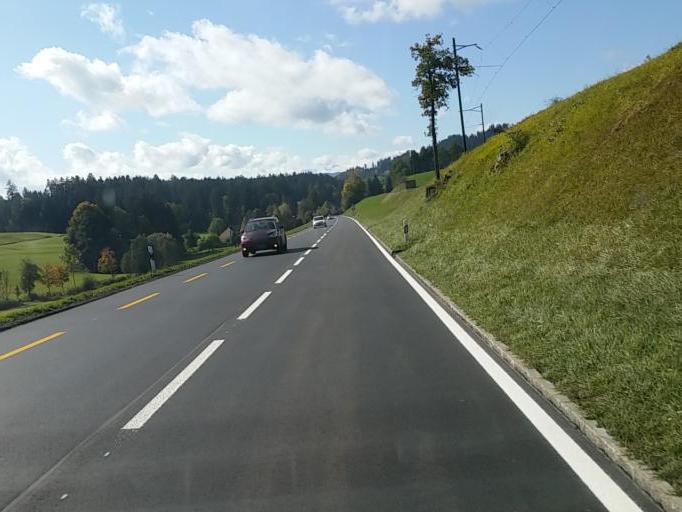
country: CH
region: Bern
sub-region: Emmental District
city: Sumiswald
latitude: 47.0495
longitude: 7.7480
